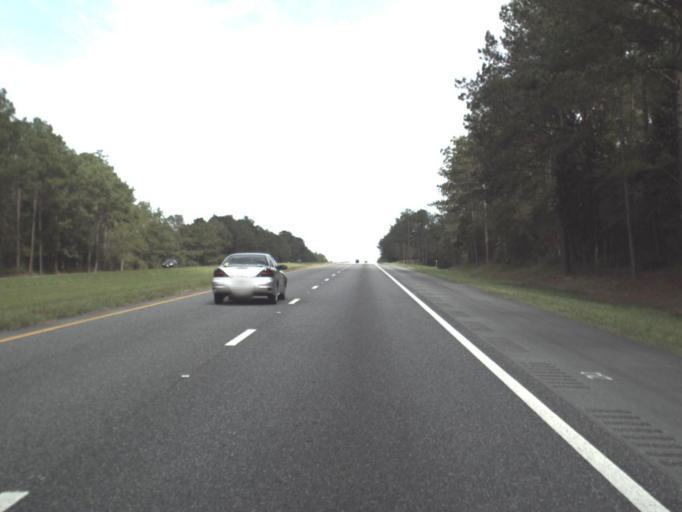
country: US
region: Florida
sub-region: Walton County
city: DeFuniak Springs
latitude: 30.6908
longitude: -86.0621
